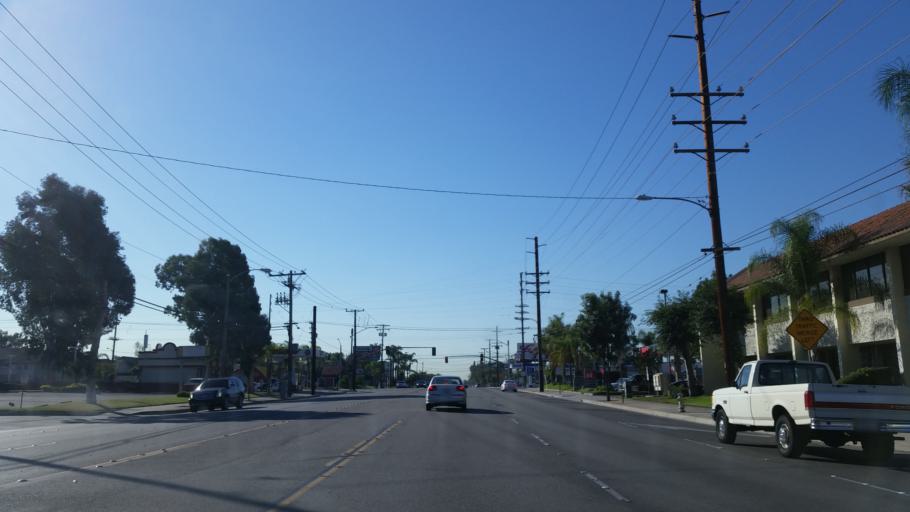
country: US
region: California
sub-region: Orange County
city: Buena Park
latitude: 33.8483
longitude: -117.9762
